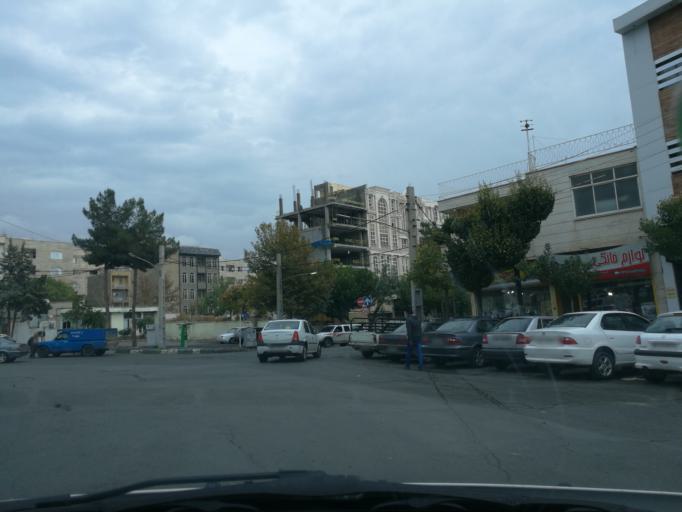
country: IR
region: Alborz
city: Karaj
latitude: 35.8498
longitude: 50.9673
